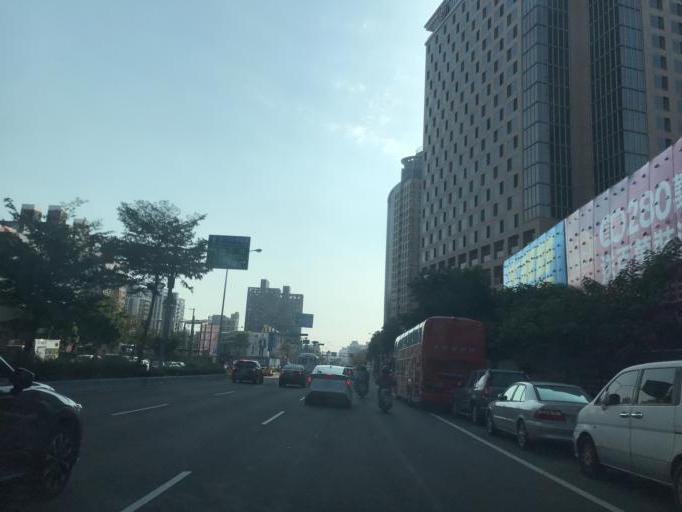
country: TW
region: Taiwan
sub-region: Hsinchu
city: Zhubei
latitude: 24.8212
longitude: 121.0293
